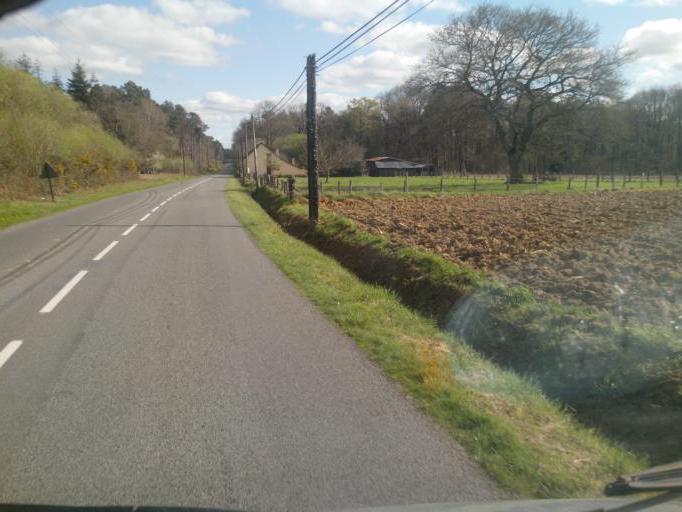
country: FR
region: Brittany
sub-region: Departement d'Ille-et-Vilaine
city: Paimpont
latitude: 48.0380
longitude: -2.1812
